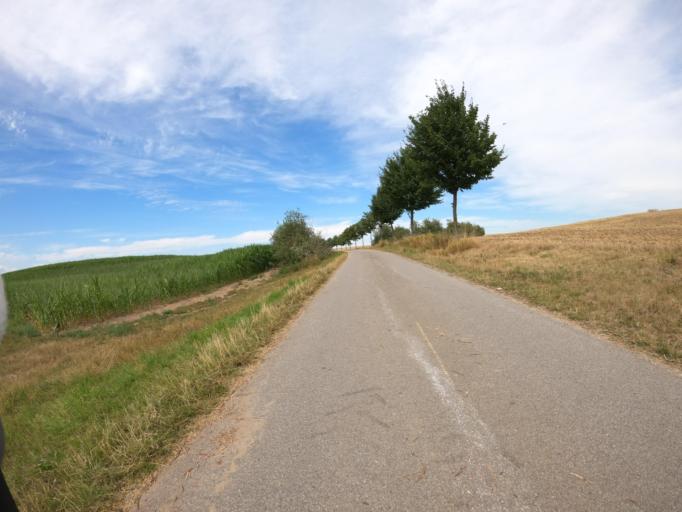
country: DE
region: Mecklenburg-Vorpommern
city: Woldegk
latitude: 53.4512
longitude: 13.4997
